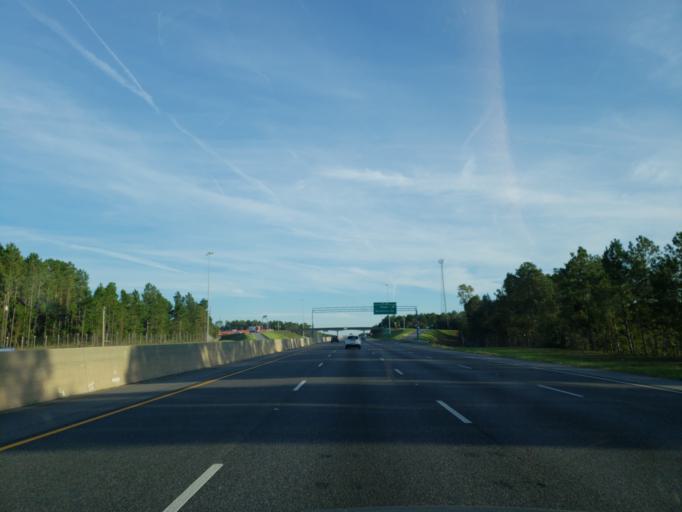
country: US
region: Georgia
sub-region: Tift County
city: Tifton
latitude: 31.5531
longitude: -83.5360
